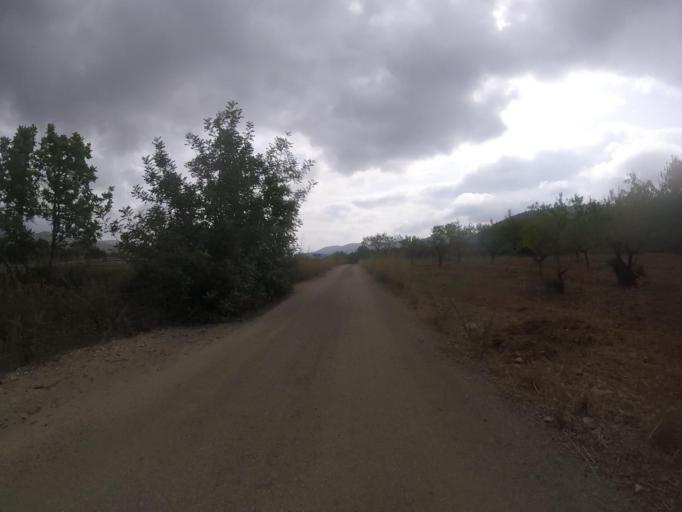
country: ES
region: Valencia
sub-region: Provincia de Castello
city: Santa Magdalena de Pulpis
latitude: 40.3470
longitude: 0.2899
